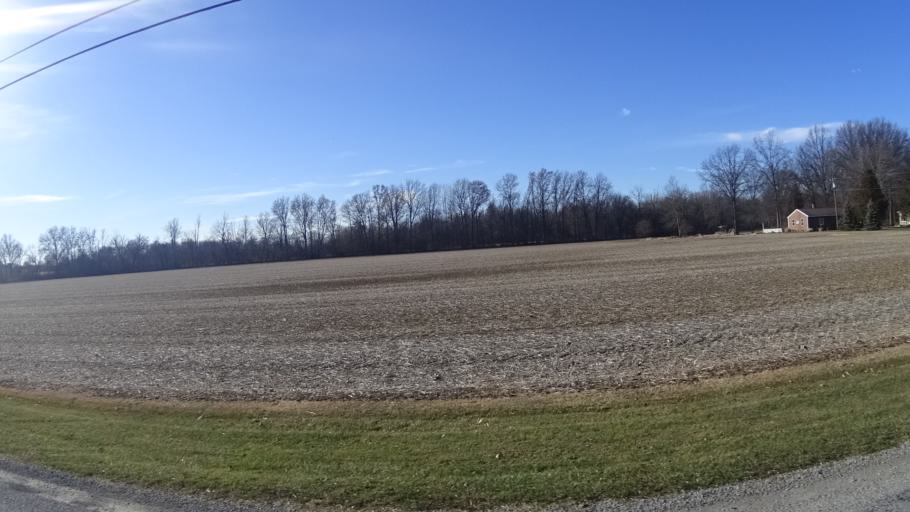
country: US
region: Ohio
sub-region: Lorain County
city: Vermilion-on-the-Lake
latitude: 41.3783
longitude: -82.3300
